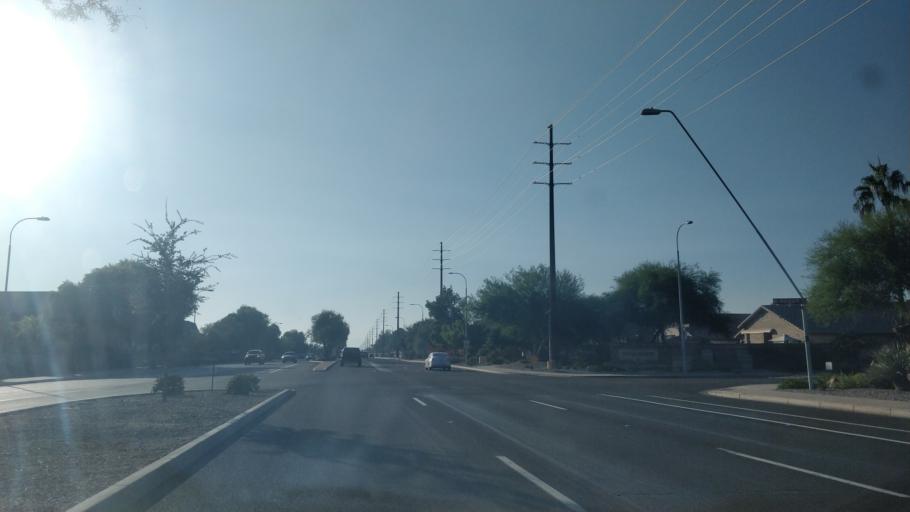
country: US
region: Arizona
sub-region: Maricopa County
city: Chandler
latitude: 33.2766
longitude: -111.8480
